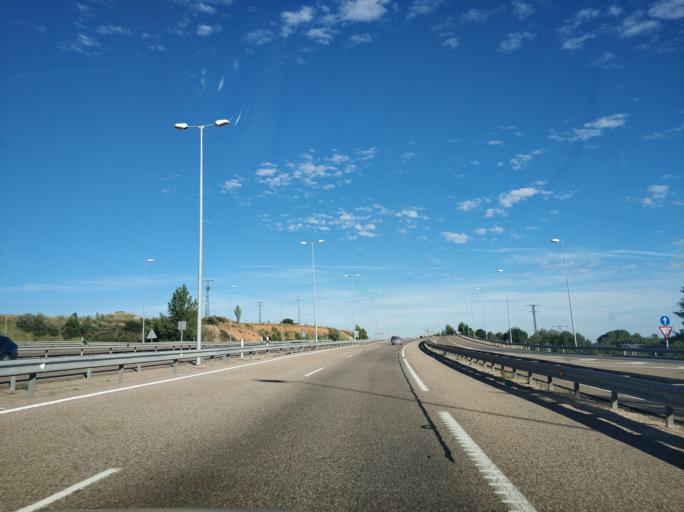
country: ES
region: Castille and Leon
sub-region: Provincia de Leon
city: Valverde de la Virgen
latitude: 42.5673
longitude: -5.6520
